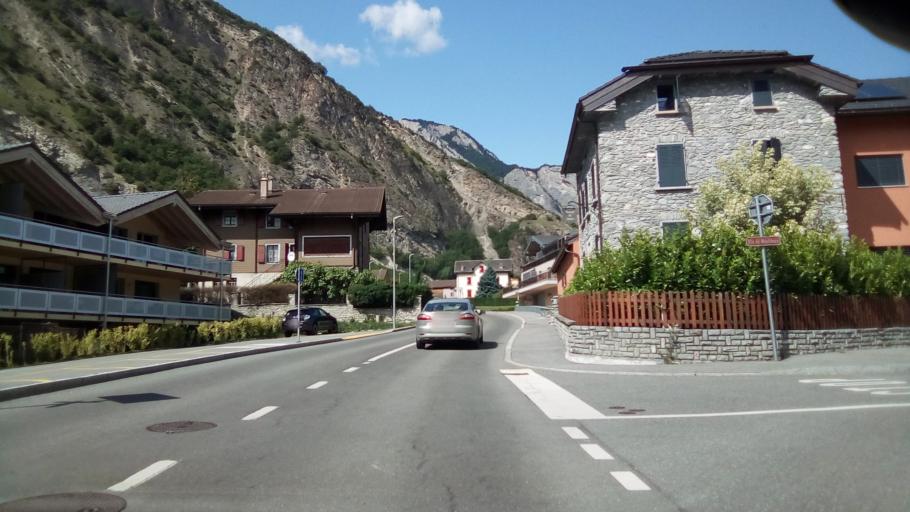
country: CH
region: Valais
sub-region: Martigny District
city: Leytron
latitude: 46.1887
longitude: 7.2098
